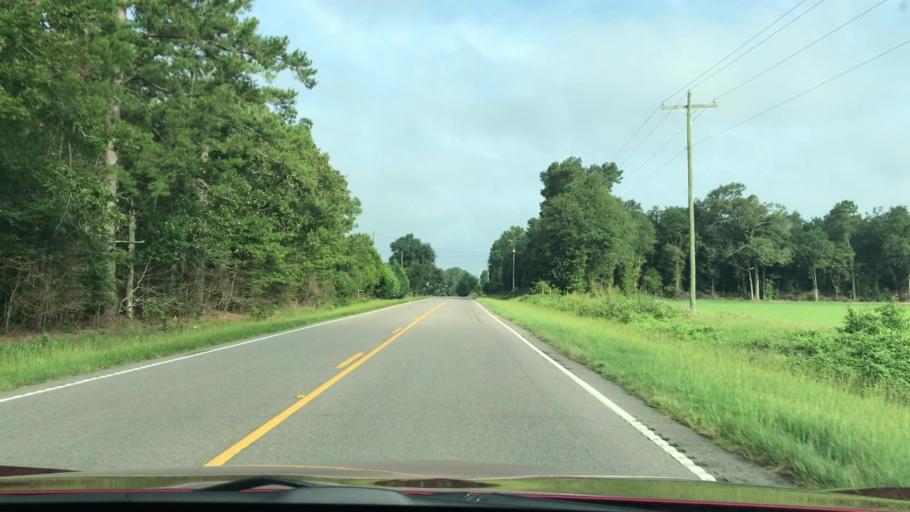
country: US
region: South Carolina
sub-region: Lexington County
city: Leesville
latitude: 33.6834
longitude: -81.4504
